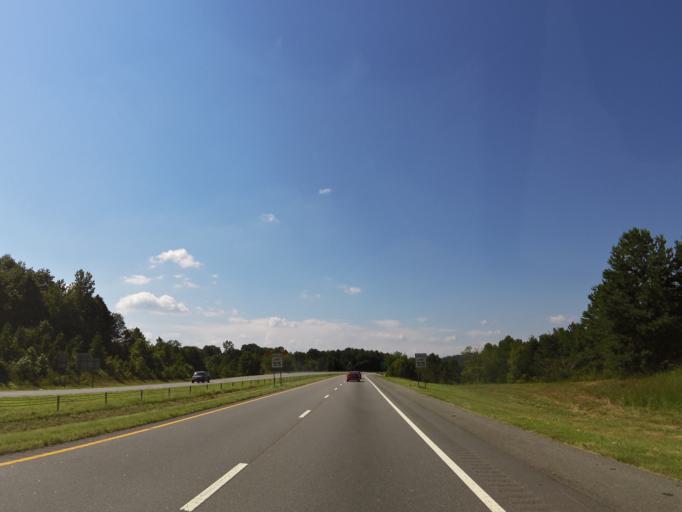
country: US
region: North Carolina
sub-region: Catawba County
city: Mountain View
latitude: 35.6878
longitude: -81.3474
